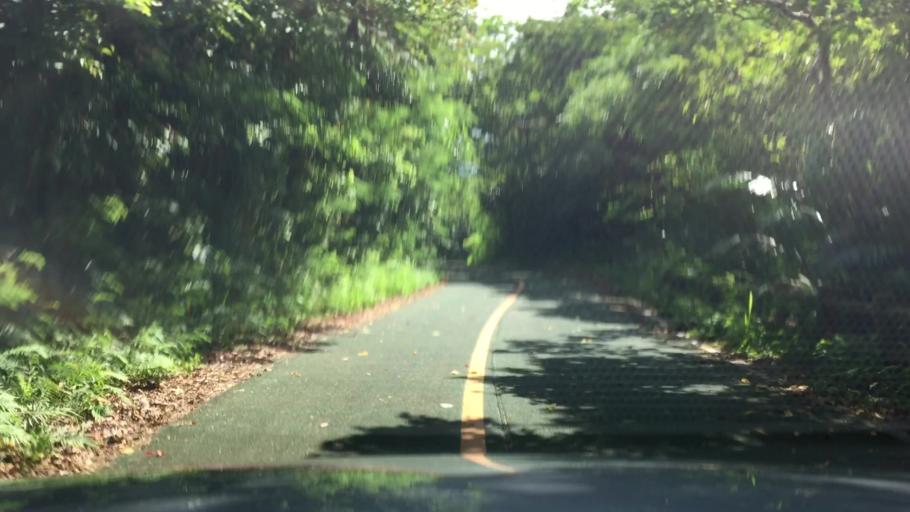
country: JP
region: Okinawa
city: Ishigaki
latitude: 24.3841
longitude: 124.1716
